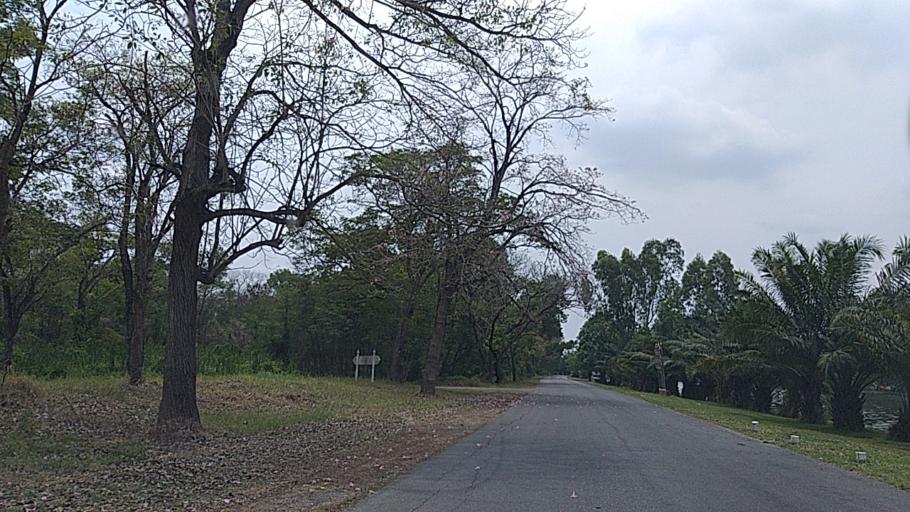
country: TH
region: Bangkok
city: Thawi Watthana
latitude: 13.7800
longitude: 100.3108
